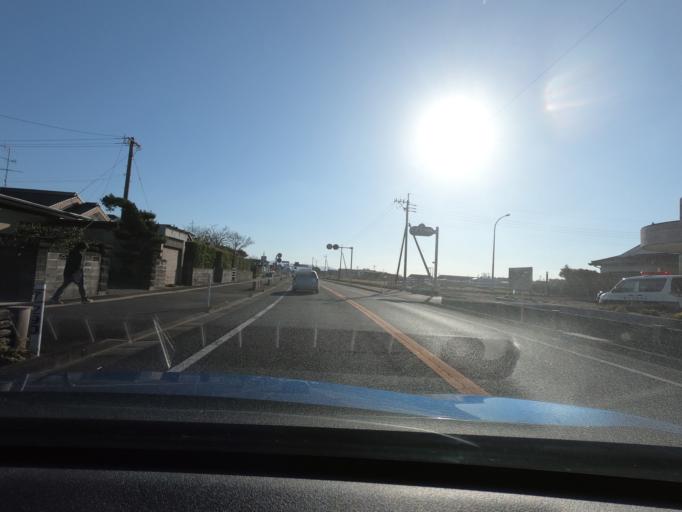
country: JP
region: Kagoshima
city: Izumi
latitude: 32.1282
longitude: 130.3441
